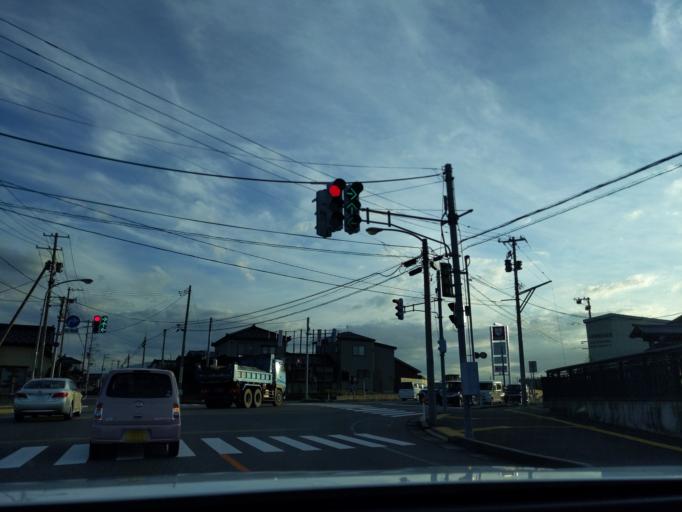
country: JP
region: Niigata
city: Kashiwazaki
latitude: 37.3843
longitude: 138.5690
